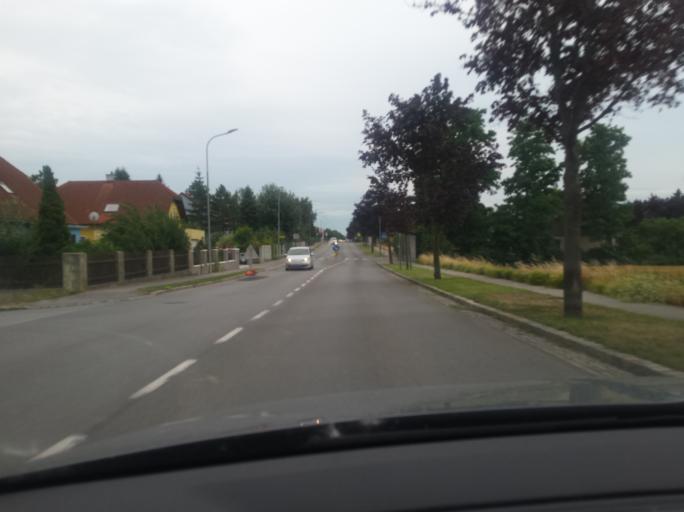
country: AT
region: Lower Austria
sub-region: Politischer Bezirk Ganserndorf
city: Deutsch-Wagram
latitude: 48.3175
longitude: 16.5782
